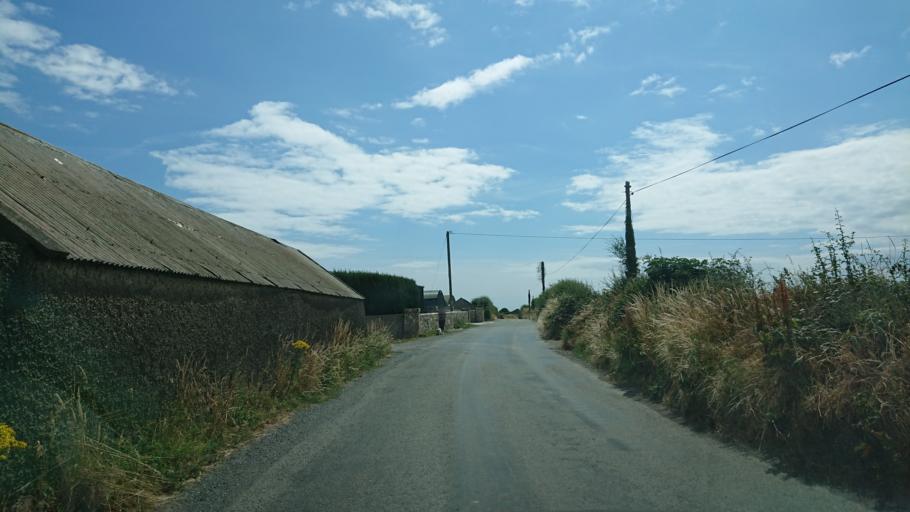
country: IE
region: Munster
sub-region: Waterford
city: Portlaw
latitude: 52.1855
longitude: -7.3325
